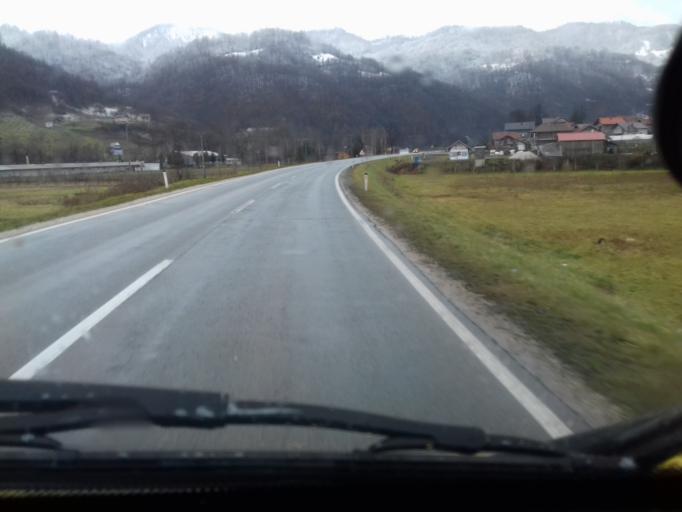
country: BA
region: Federation of Bosnia and Herzegovina
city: Zeljezno Polje
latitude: 44.3502
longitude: 17.9861
